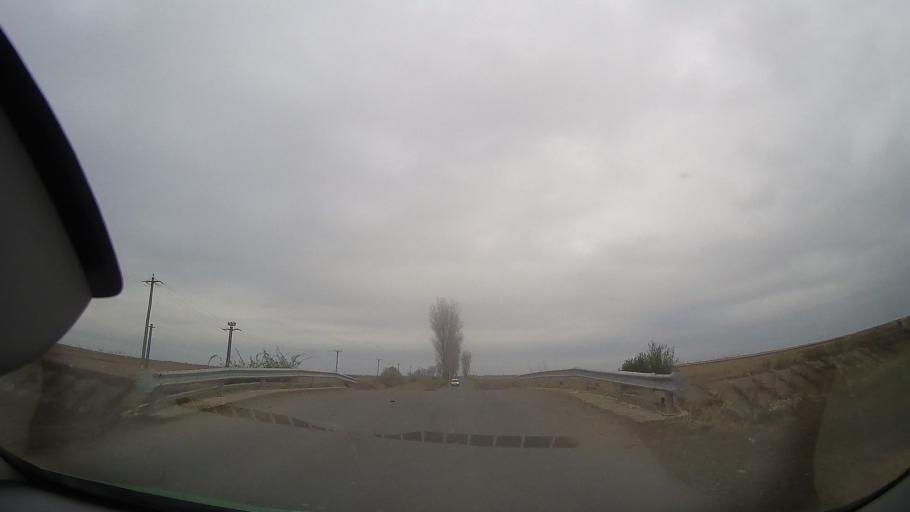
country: RO
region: Braila
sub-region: Comuna Rosiori
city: Rosiori
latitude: 44.8190
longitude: 27.3594
